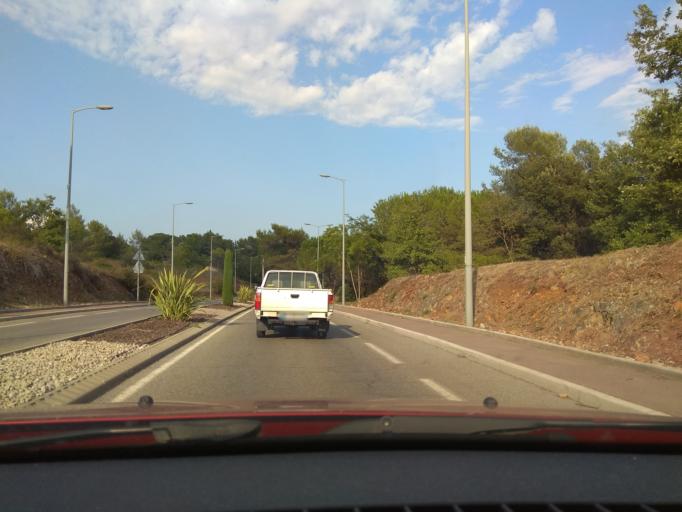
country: FR
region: Provence-Alpes-Cote d'Azur
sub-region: Departement des Alpes-Maritimes
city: Le Rouret
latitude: 43.6635
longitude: 7.0397
